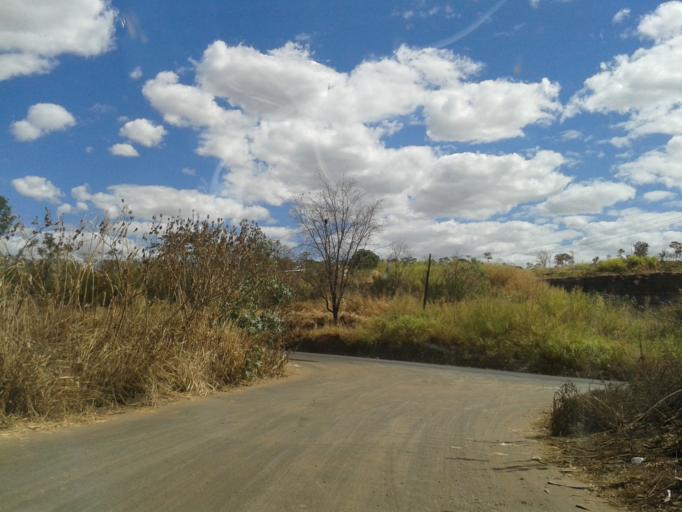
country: BR
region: Minas Gerais
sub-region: Ituiutaba
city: Ituiutaba
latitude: -18.9596
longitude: -49.4710
